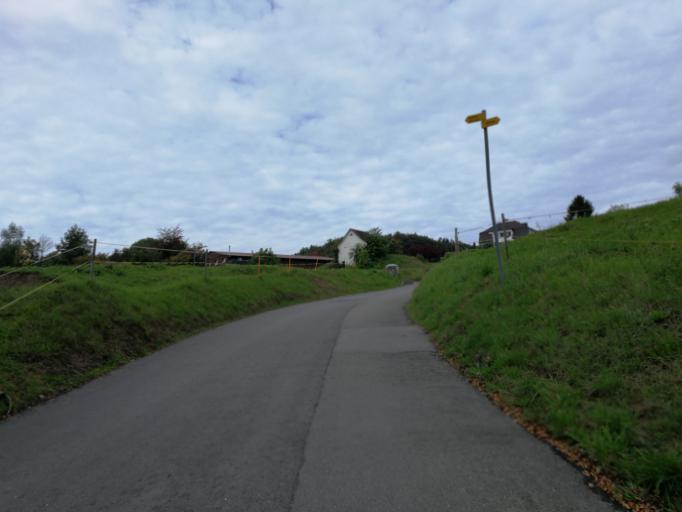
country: CH
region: Zurich
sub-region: Bezirk Meilen
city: Stafa
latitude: 47.2532
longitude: 8.7182
